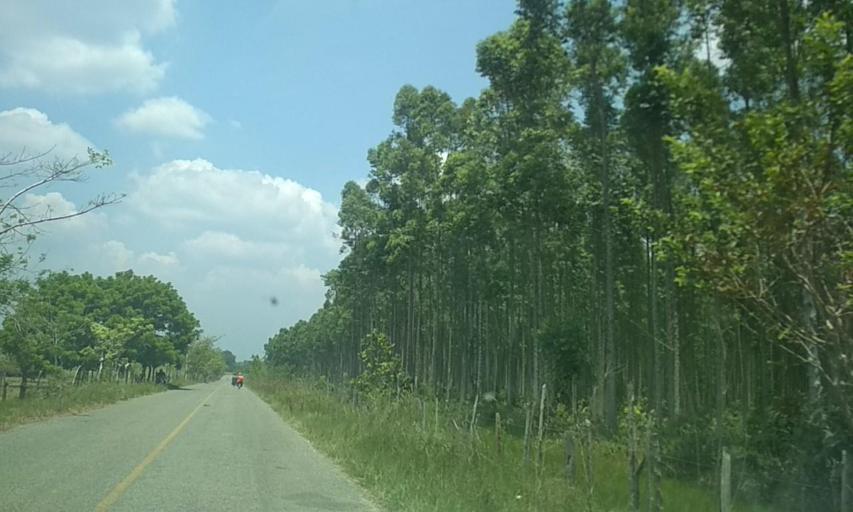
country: MX
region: Tabasco
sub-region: Huimanguillo
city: Francisco Rueda
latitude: 17.8385
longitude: -93.9037
